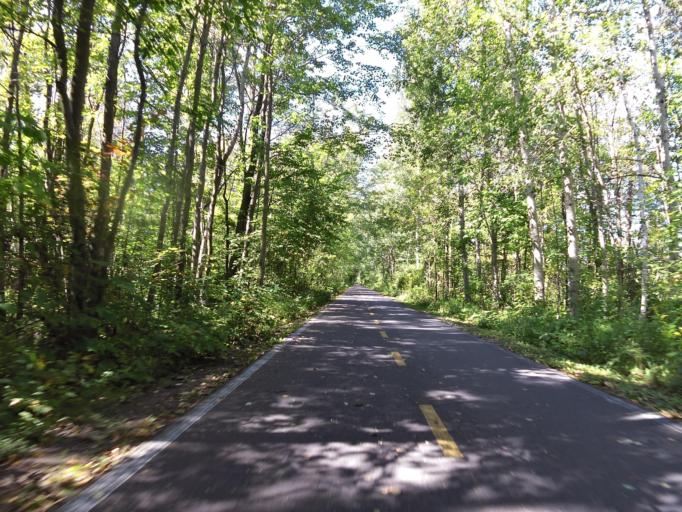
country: CA
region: Ontario
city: Bourget
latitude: 45.2692
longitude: -75.3183
